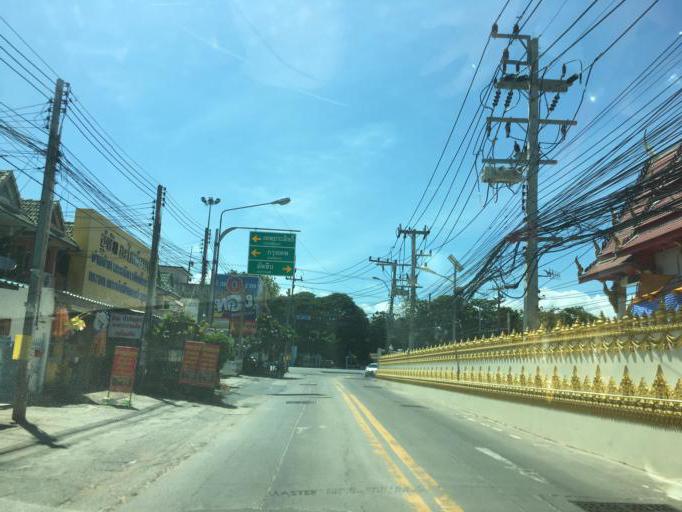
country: TH
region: Chon Buri
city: Phatthaya
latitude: 12.8897
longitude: 100.8966
